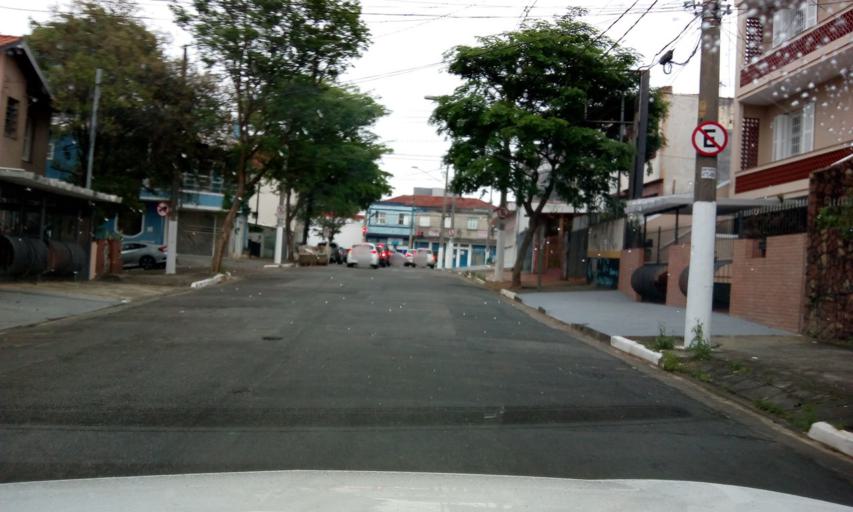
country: BR
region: Sao Paulo
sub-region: Sao Paulo
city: Sao Paulo
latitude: -23.5835
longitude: -46.6267
